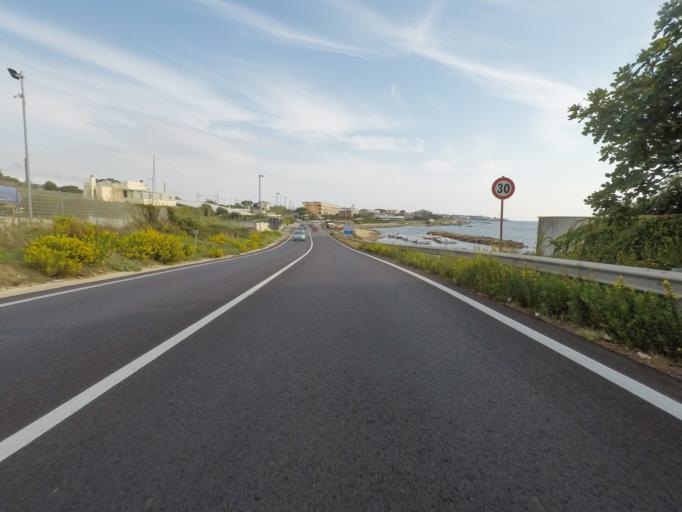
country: IT
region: Latium
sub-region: Citta metropolitana di Roma Capitale
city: Santa Marinella
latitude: 42.0456
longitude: 11.8249
